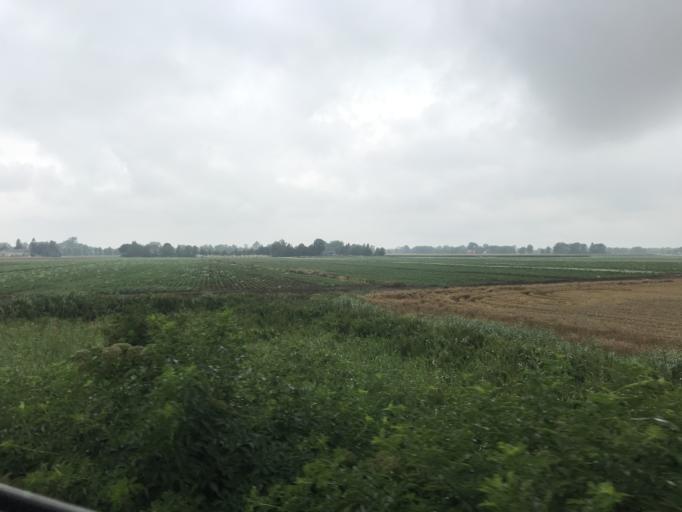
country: PL
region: Warmian-Masurian Voivodeship
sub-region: Powiat elblaski
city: Gronowo Elblaskie
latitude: 54.1155
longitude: 19.3504
